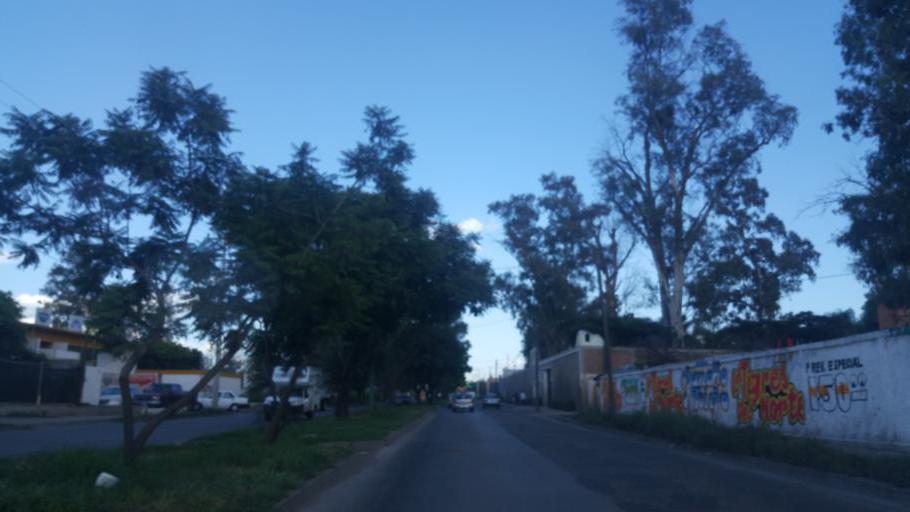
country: MX
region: Guanajuato
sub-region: Leon
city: San Jose de Duran (Los Troncoso)
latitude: 21.0941
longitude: -101.6906
